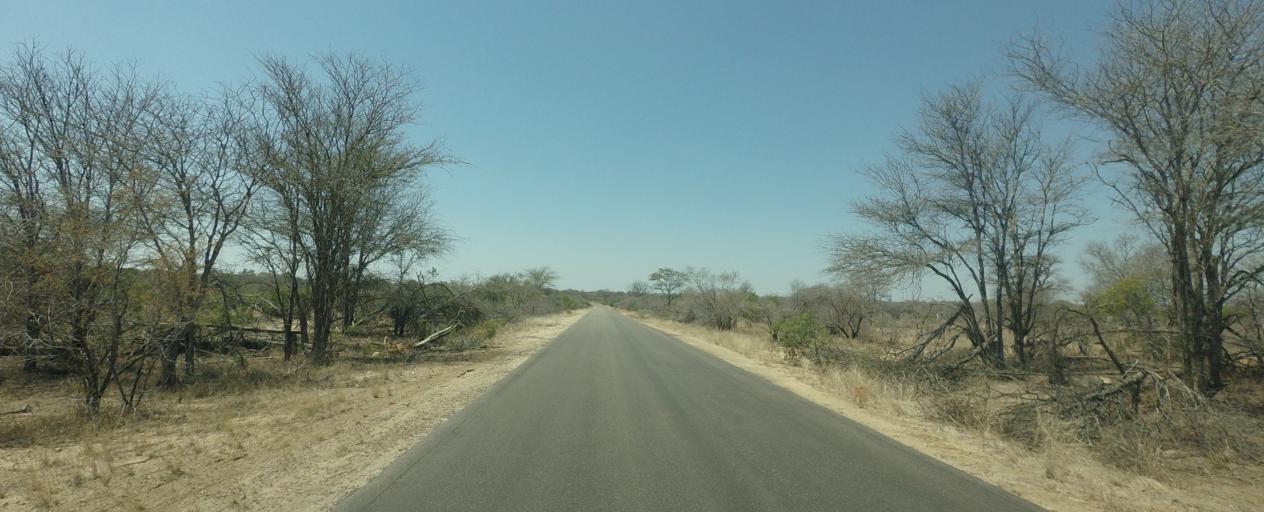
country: ZA
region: Limpopo
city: Thulamahashi
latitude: -24.4246
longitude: 31.5068
